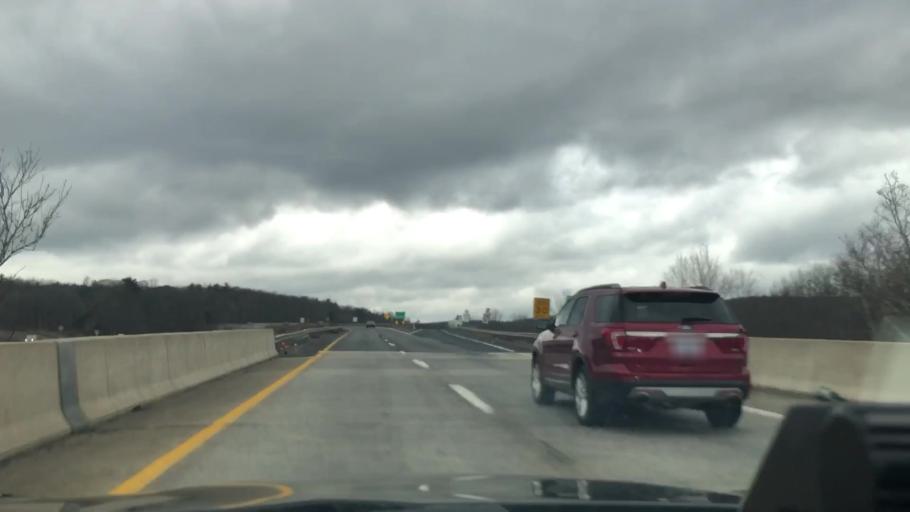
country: US
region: Pennsylvania
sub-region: Monroe County
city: Tannersville
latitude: 41.0517
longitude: -75.3163
